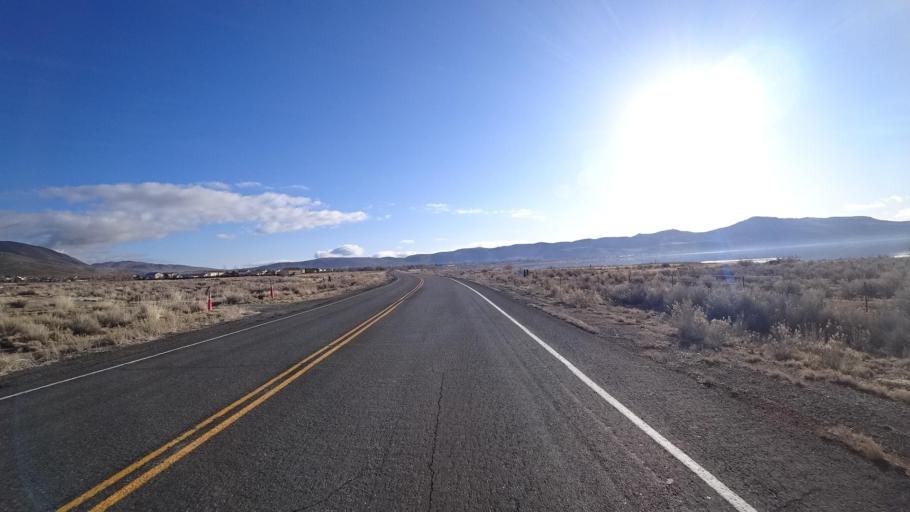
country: US
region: Nevada
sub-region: Washoe County
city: Cold Springs
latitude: 39.6716
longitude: -119.9885
